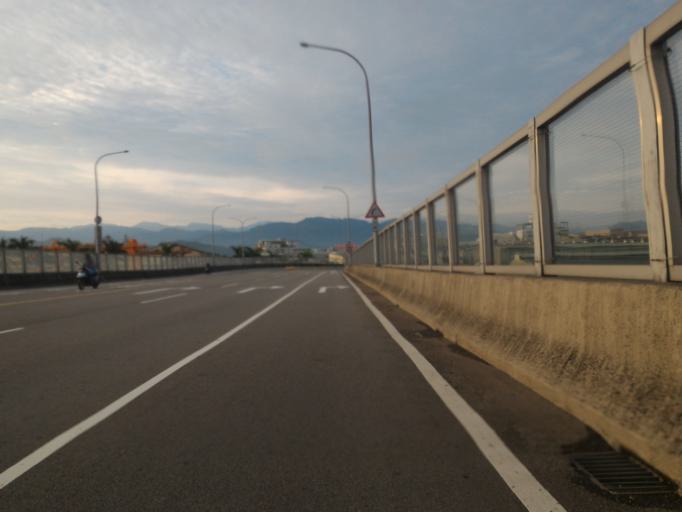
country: TW
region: Taiwan
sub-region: Taoyuan
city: Taoyuan
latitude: 24.9659
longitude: 121.3943
